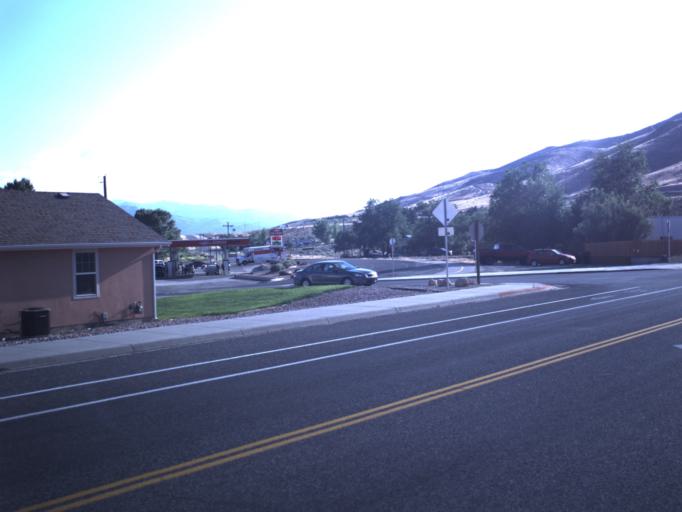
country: US
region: Utah
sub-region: Sevier County
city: Monroe
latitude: 38.6830
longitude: -112.1522
